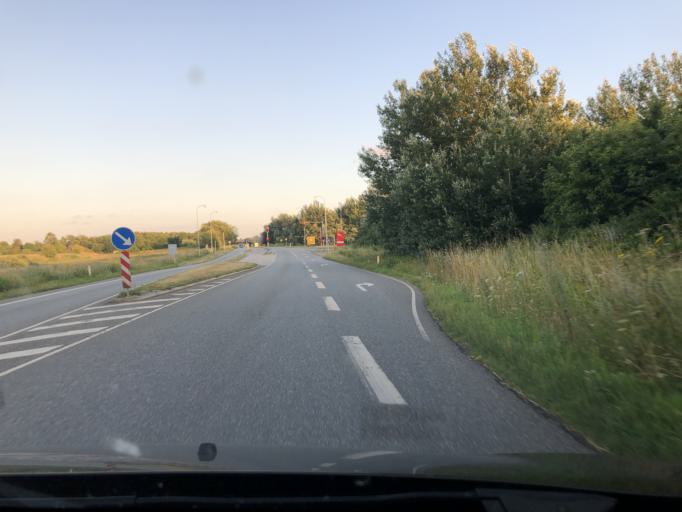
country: DK
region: South Denmark
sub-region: Fredericia Kommune
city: Snoghoj
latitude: 55.5417
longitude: 9.6844
